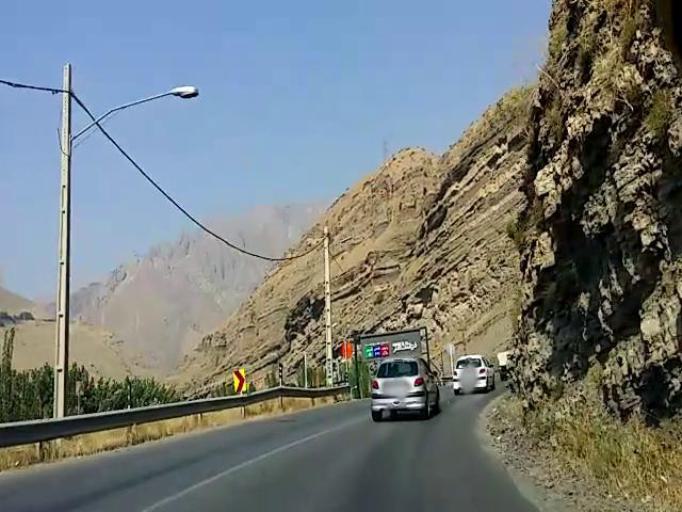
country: IR
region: Alborz
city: Karaj
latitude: 35.9398
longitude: 51.0725
